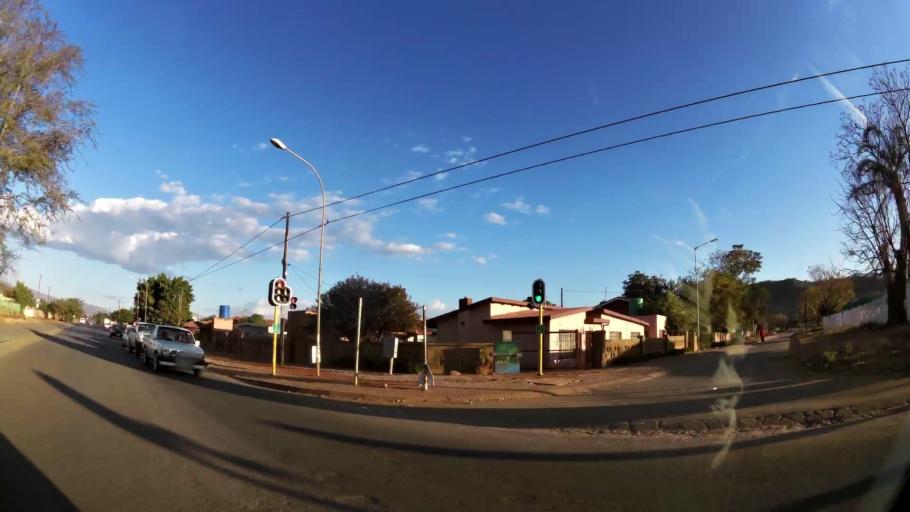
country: ZA
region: Limpopo
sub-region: Waterberg District Municipality
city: Mokopane
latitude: -24.1497
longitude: 28.9800
